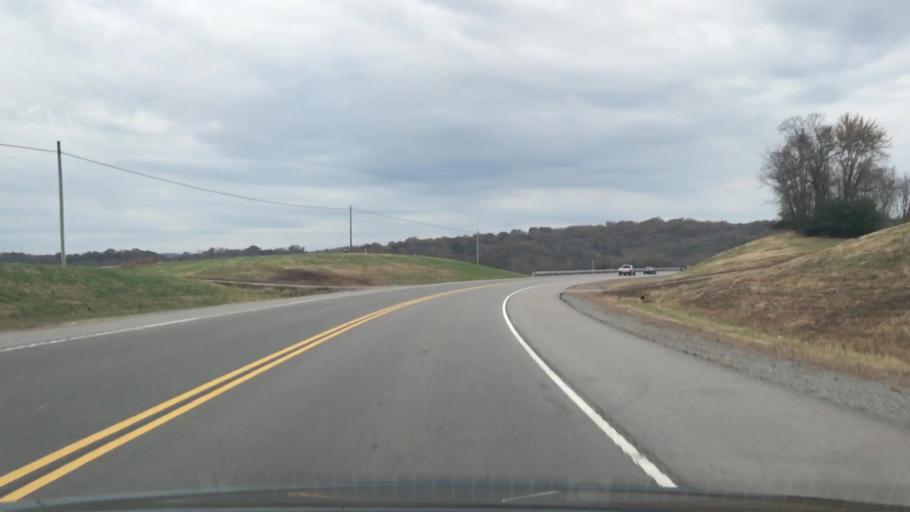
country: US
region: Tennessee
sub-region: Trousdale County
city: Hartsville
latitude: 36.3622
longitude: -86.1748
